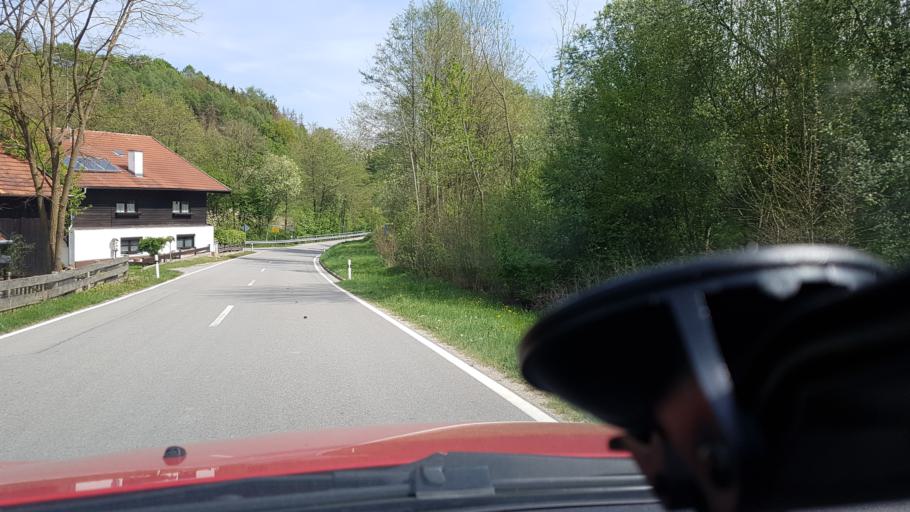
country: DE
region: Bavaria
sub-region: Lower Bavaria
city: Stubenberg
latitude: 48.3349
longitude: 13.0965
